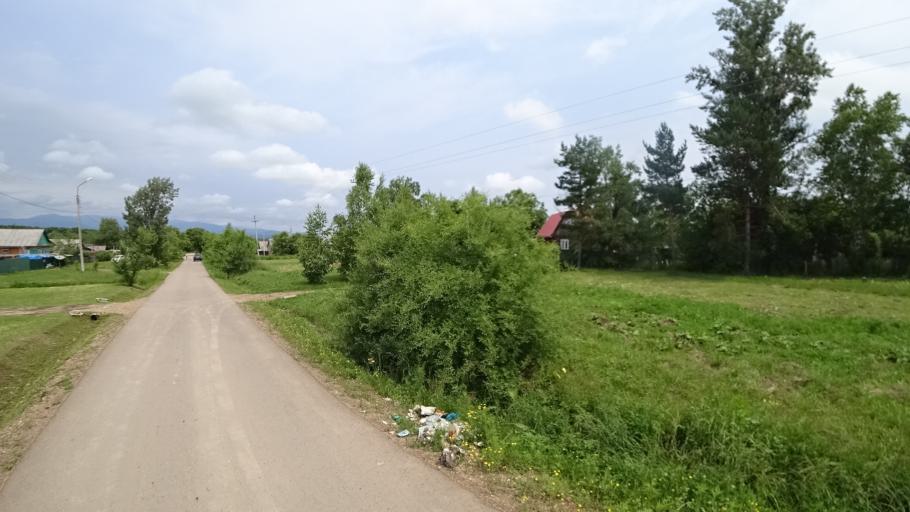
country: RU
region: Primorskiy
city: Novosysoyevka
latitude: 44.2370
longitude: 133.3585
